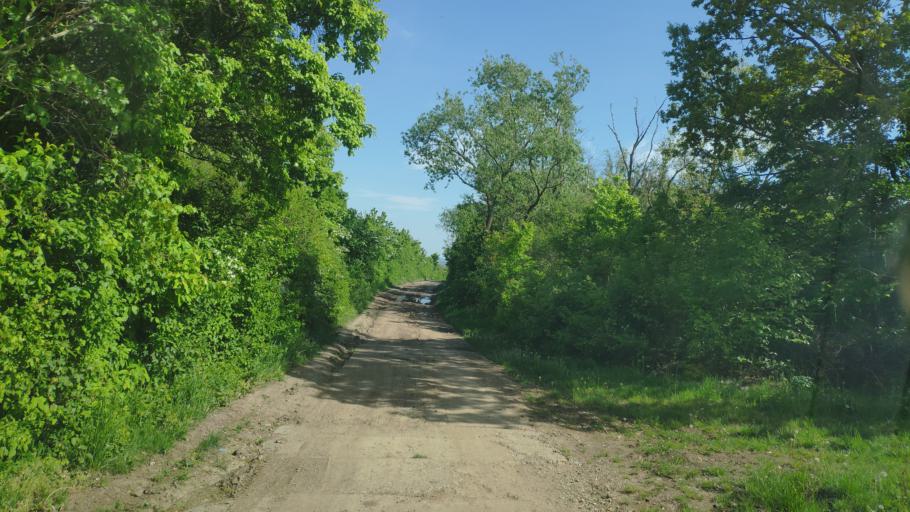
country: SK
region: Kosicky
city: Secovce
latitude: 48.6882
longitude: 21.6045
